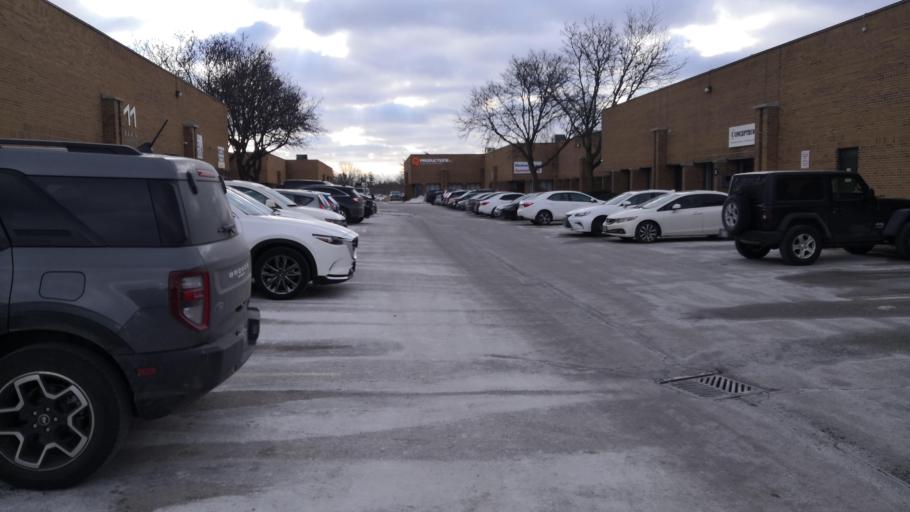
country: CA
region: Ontario
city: Concord
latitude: 43.7655
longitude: -79.4706
